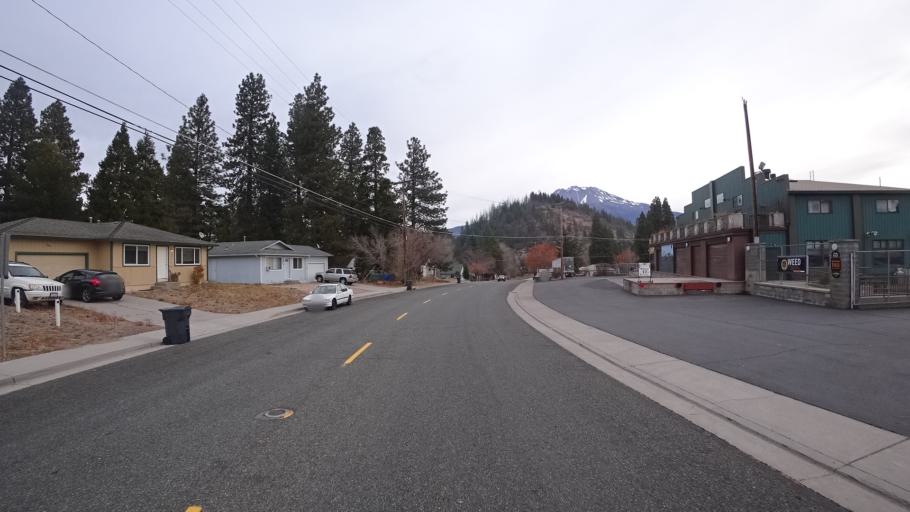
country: US
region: California
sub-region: Siskiyou County
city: Weed
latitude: 41.4164
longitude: -122.3874
